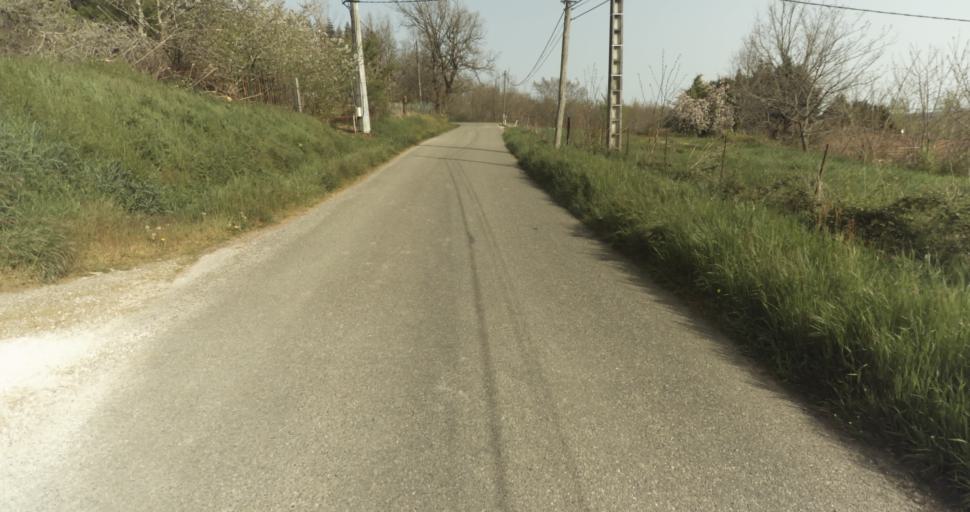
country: FR
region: Midi-Pyrenees
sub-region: Departement du Tarn-et-Garonne
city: Moissac
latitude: 44.1309
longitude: 1.0972
